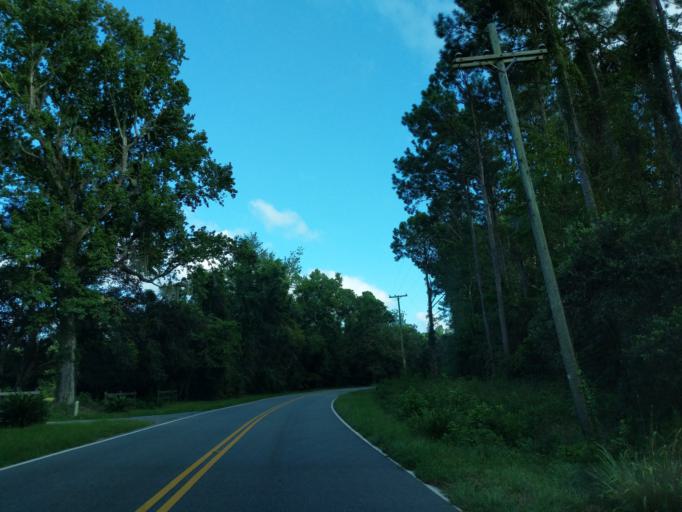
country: US
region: South Carolina
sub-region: Charleston County
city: Awendaw
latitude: 33.0965
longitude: -79.4665
